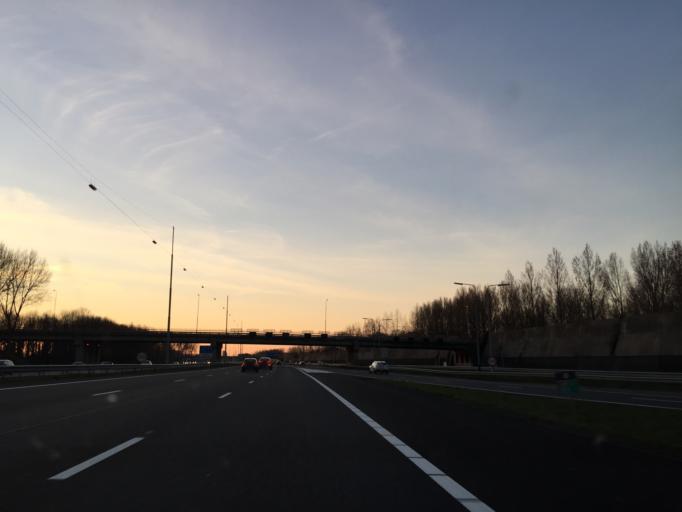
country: NL
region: South Holland
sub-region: Gemeente Ridderkerk
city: Ridderkerk
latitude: 51.8595
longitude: 4.5949
